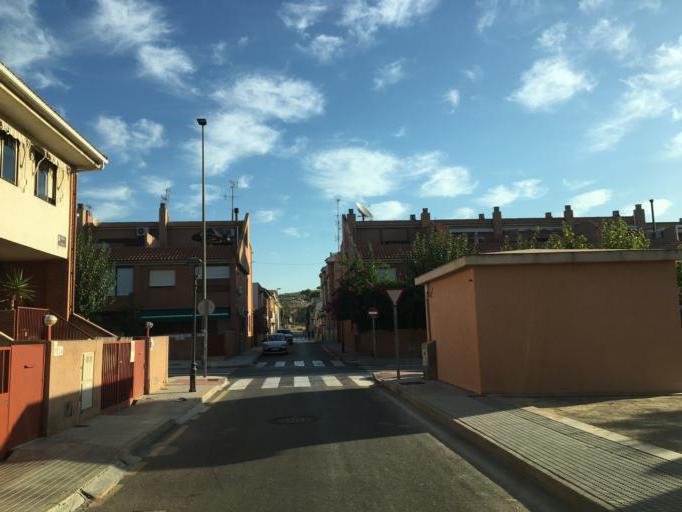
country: ES
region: Murcia
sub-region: Murcia
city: Murcia
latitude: 38.0135
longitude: -1.1527
